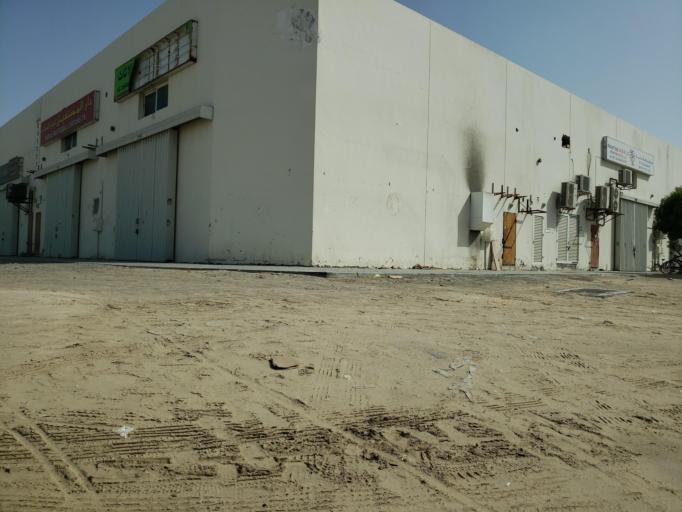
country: AE
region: Ash Shariqah
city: Sharjah
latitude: 25.3289
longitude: 55.4006
